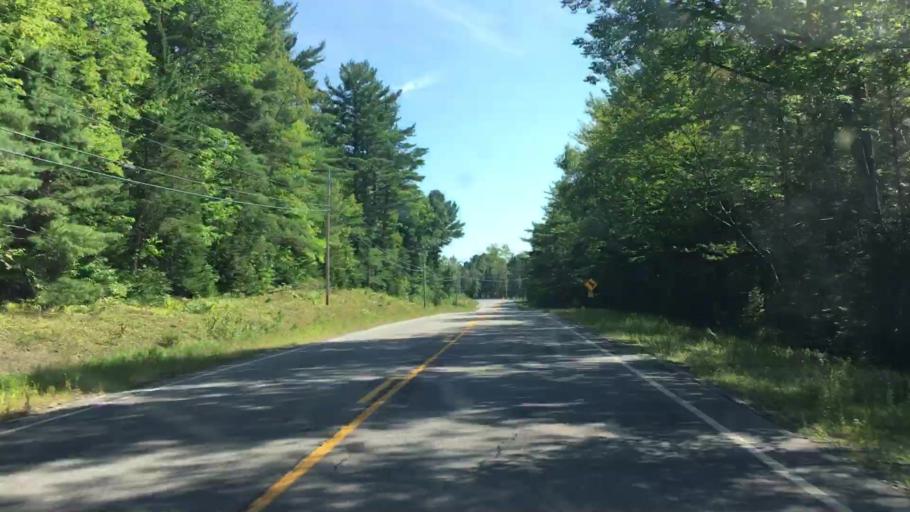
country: US
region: Maine
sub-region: Piscataquis County
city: Milo
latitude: 45.1909
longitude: -68.8978
